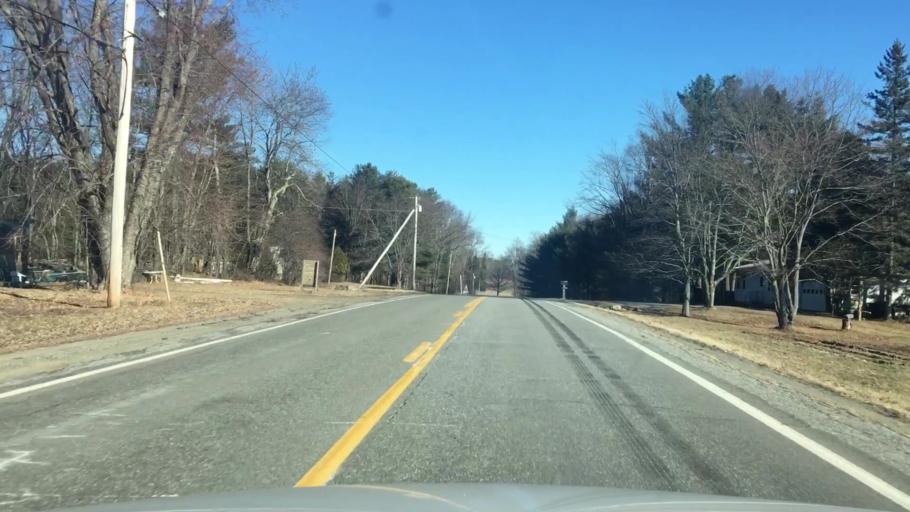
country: US
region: Maine
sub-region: Kennebec County
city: Benton
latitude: 44.5761
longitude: -69.5622
